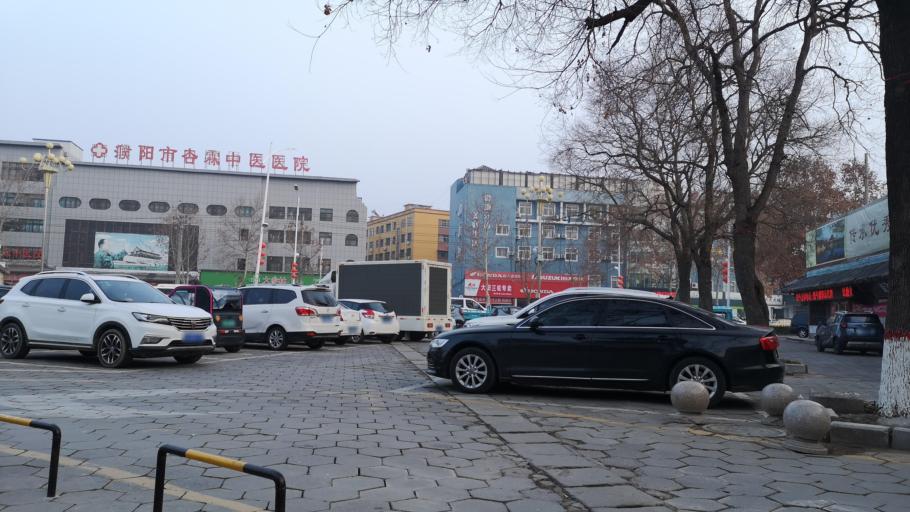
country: CN
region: Henan Sheng
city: Puyang
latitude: 35.7521
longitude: 115.0301
